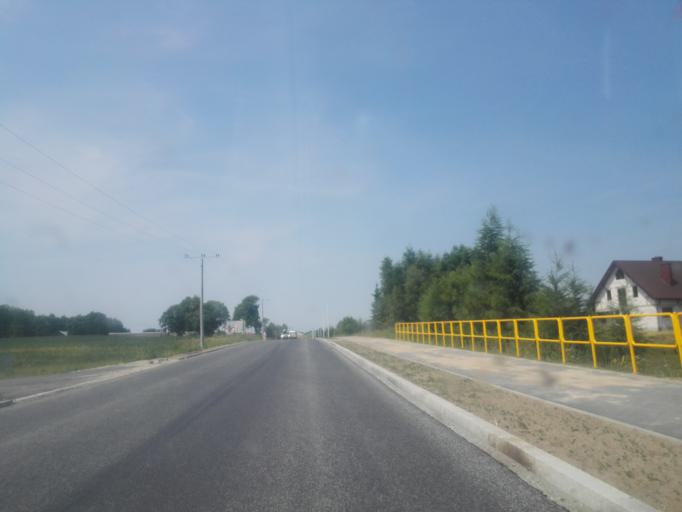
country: PL
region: Podlasie
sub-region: Suwalki
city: Suwalki
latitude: 54.0860
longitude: 22.9999
